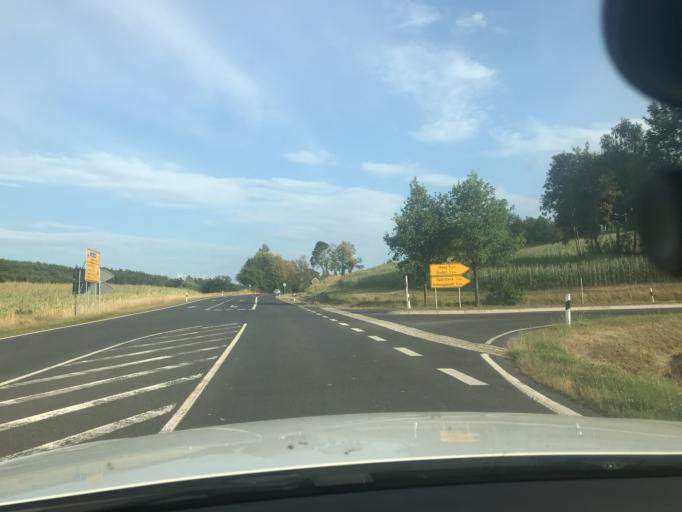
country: DE
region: Bavaria
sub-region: Upper Franconia
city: Creussen
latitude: 49.8586
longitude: 11.6167
